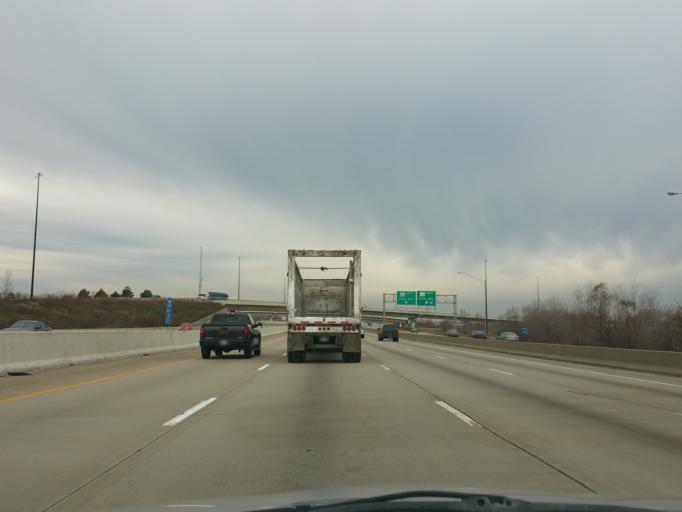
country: US
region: Indiana
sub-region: Lake County
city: Highland
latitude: 41.5700
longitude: -87.4265
